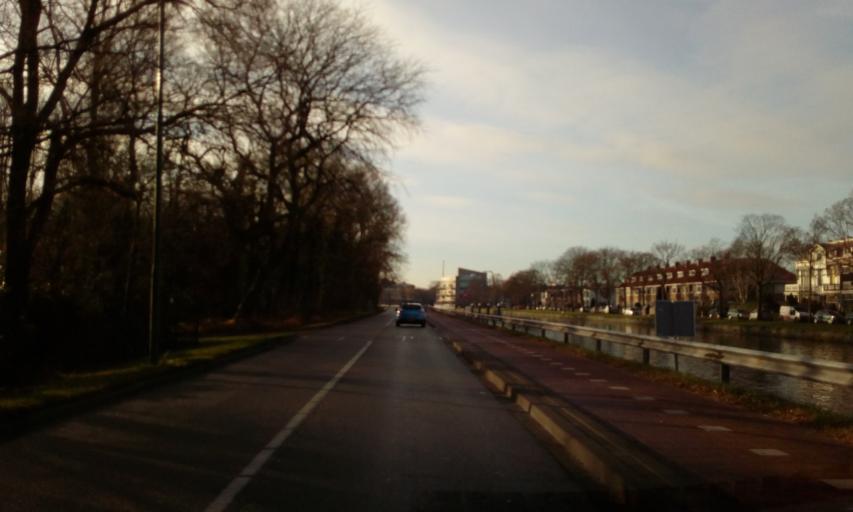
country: NL
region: South Holland
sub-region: Gemeente Leidschendam-Voorburg
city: Voorburg
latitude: 52.0550
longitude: 4.3464
